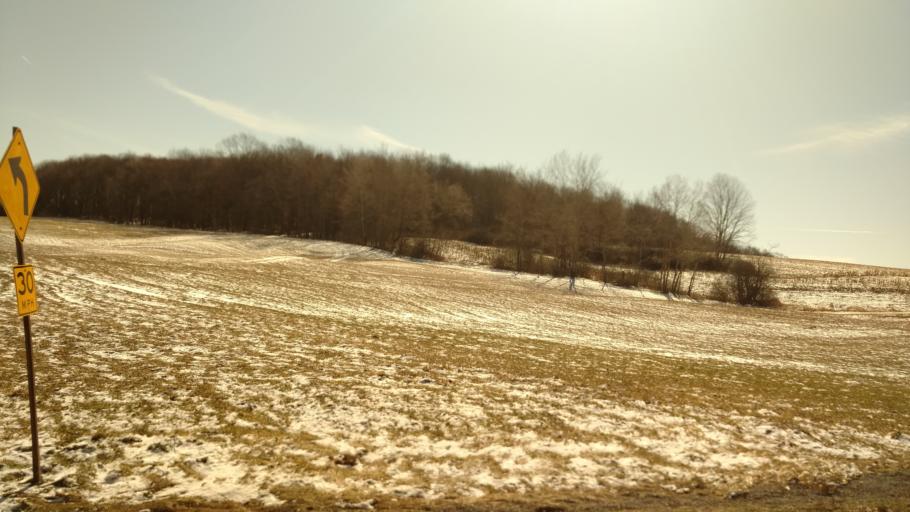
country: US
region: New York
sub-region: Allegany County
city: Wellsville
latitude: 42.0871
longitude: -77.9611
